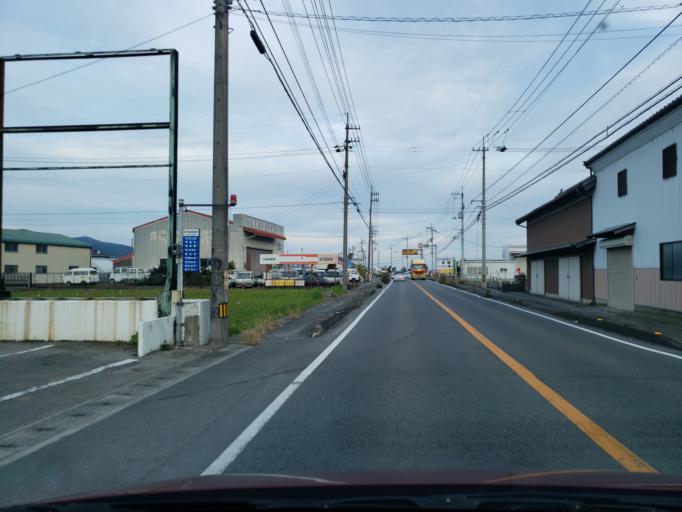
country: JP
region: Tokushima
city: Kamojimacho-jogejima
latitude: 34.0945
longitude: 134.3136
